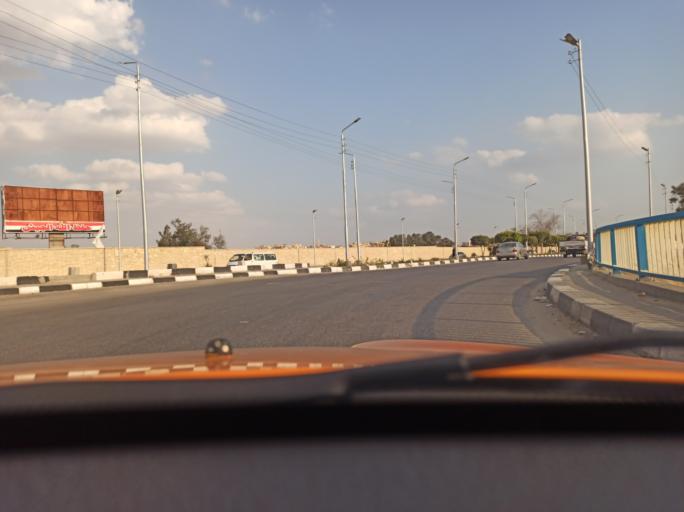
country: EG
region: Al Isma'iliyah
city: Ismailia
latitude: 30.6199
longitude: 32.2468
